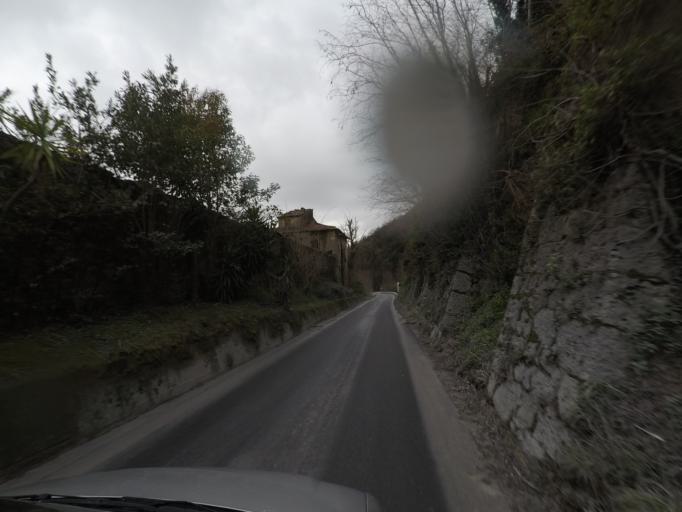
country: IT
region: Tuscany
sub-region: Provincia di Massa-Carrara
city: Carrara
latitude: 44.0849
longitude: 10.1159
